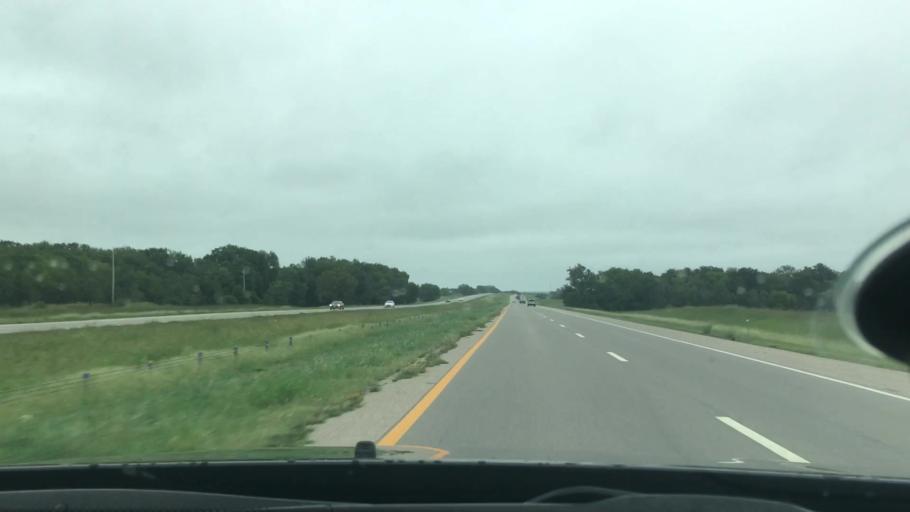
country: US
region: Oklahoma
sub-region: Okfuskee County
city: Okemah
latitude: 35.4239
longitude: -96.2768
